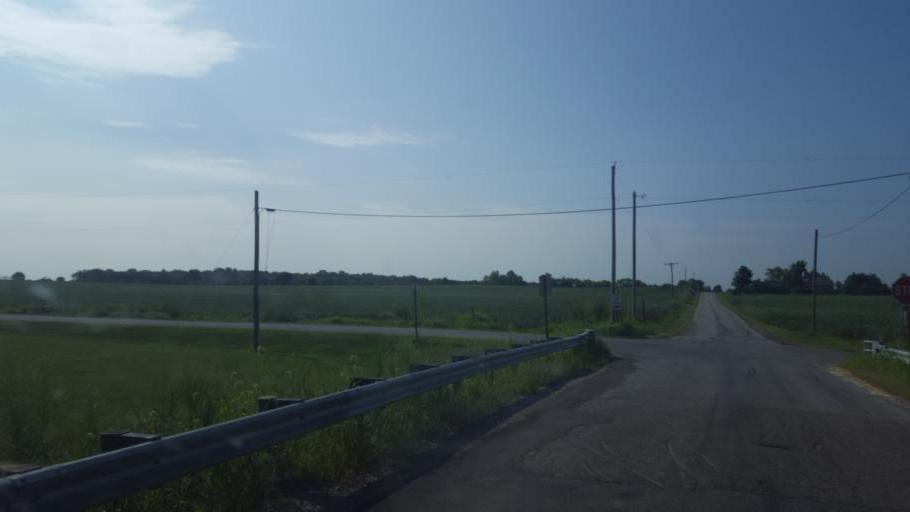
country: US
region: Ohio
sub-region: Morrow County
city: Cardington
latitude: 40.5286
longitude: -82.9195
